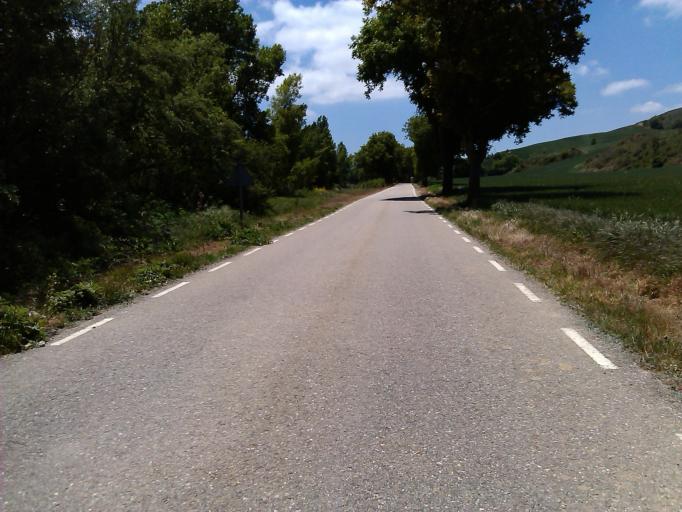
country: ES
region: Castille and Leon
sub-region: Provincia de Burgos
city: Alcocero de Mola
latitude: 42.4429
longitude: -3.3507
